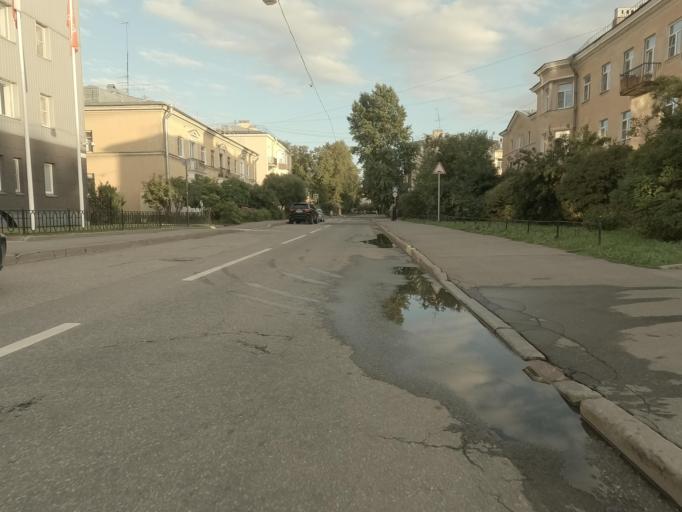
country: RU
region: St.-Petersburg
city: Admiralteisky
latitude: 59.8983
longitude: 30.2713
